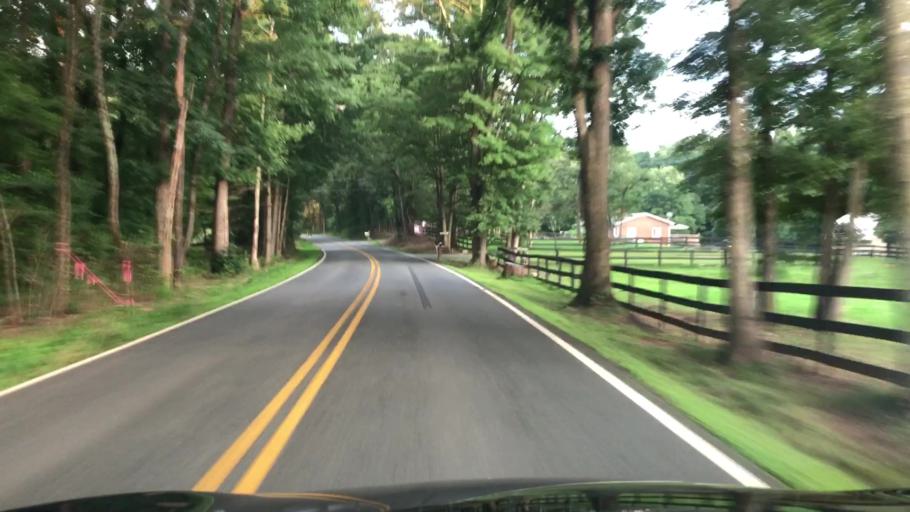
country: US
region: Virginia
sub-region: Fauquier County
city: Bealeton
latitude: 38.5383
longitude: -77.6742
